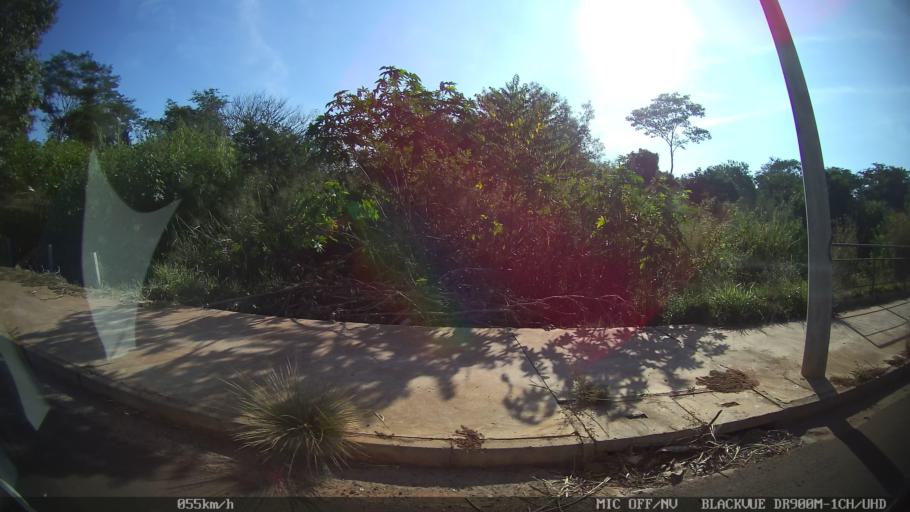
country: BR
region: Sao Paulo
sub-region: Sao Jose Do Rio Preto
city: Sao Jose do Rio Preto
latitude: -20.7647
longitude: -49.3598
